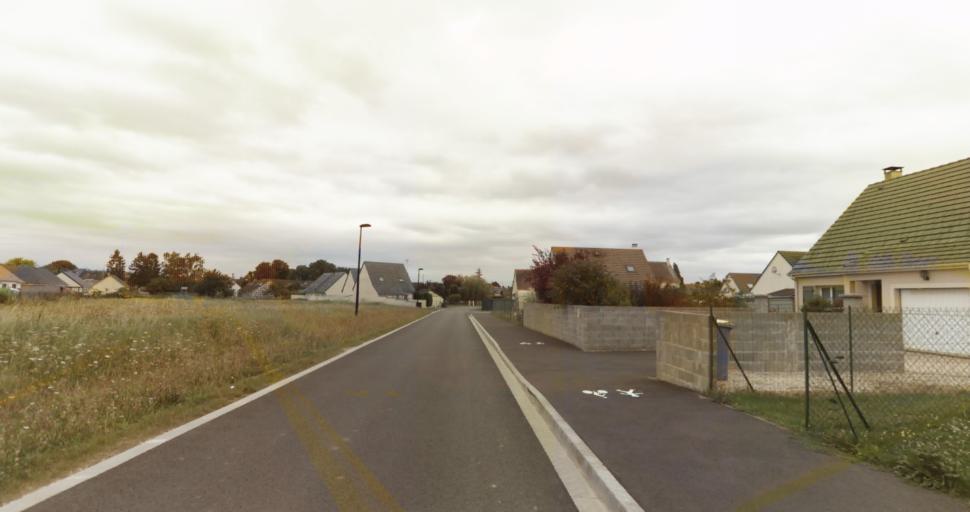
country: FR
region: Haute-Normandie
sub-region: Departement de l'Eure
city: Marcilly-sur-Eure
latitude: 48.9130
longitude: 1.2753
